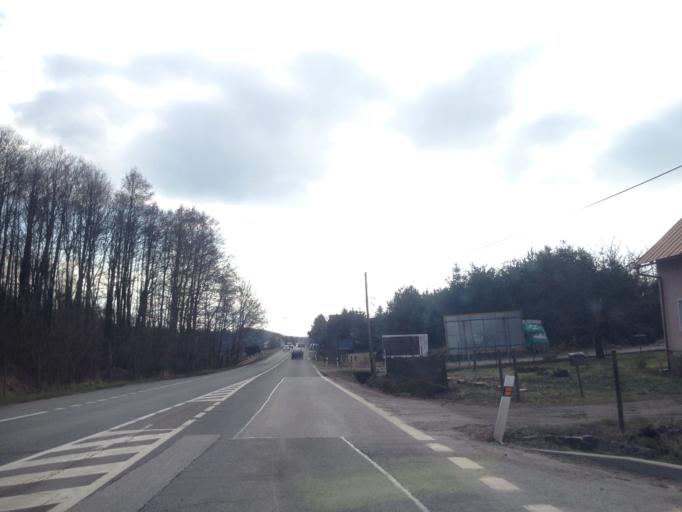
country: CZ
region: Kralovehradecky
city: Nova Paka
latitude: 50.4762
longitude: 15.5020
